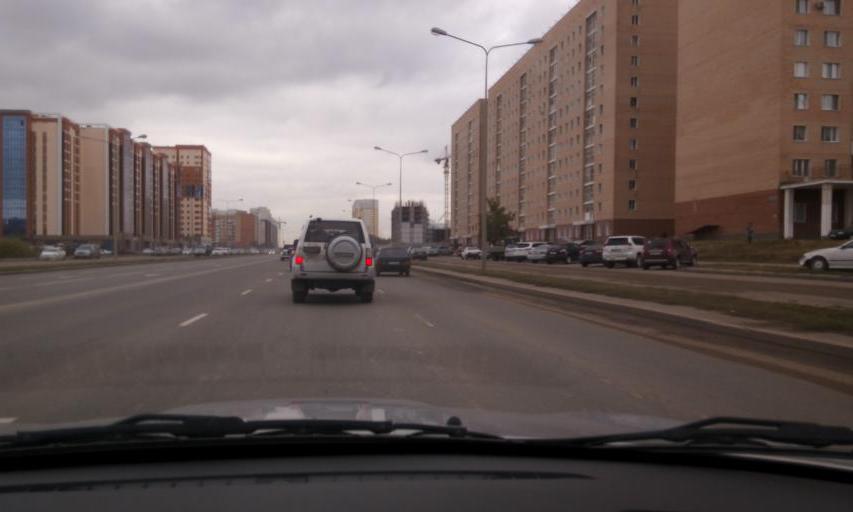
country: KZ
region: Astana Qalasy
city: Astana
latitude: 51.1273
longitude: 71.4914
